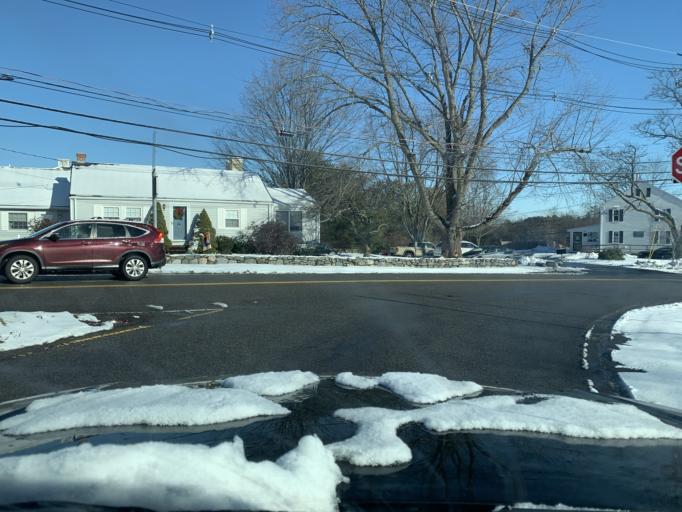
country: US
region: Massachusetts
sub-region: Essex County
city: Danvers
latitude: 42.5705
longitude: -70.9744
